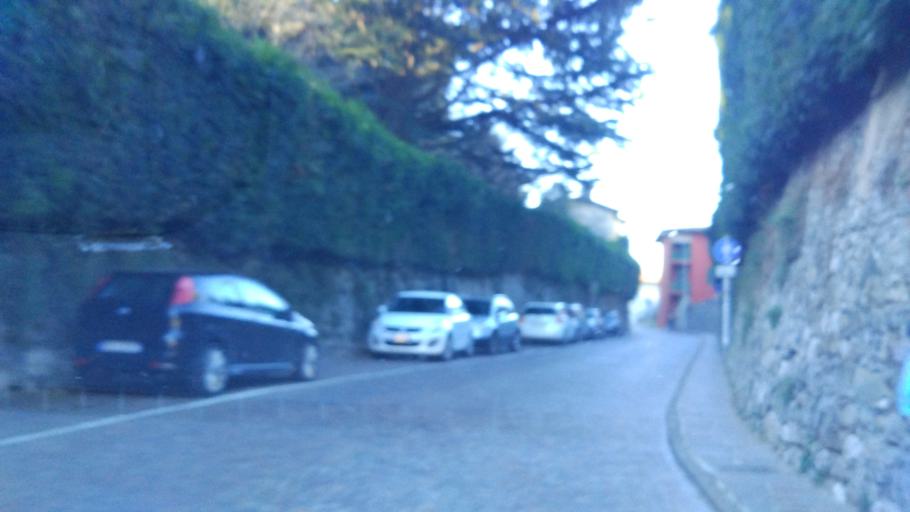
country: IT
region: Lombardy
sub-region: Provincia di Lecco
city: Malgrate
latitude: 45.8523
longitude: 9.3742
